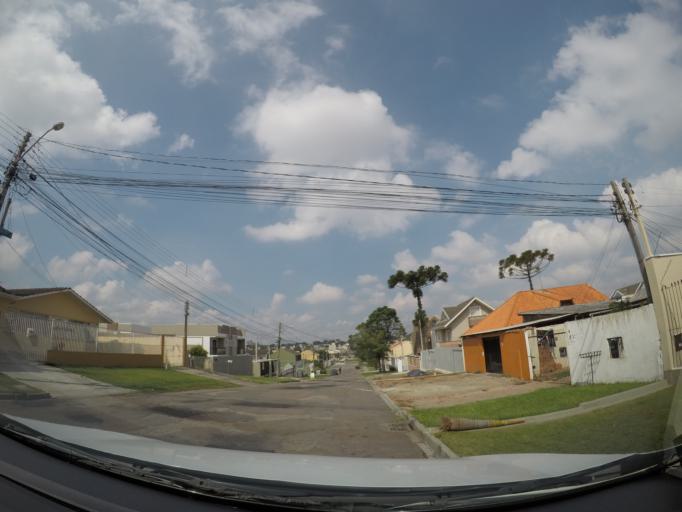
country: BR
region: Parana
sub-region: Sao Jose Dos Pinhais
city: Sao Jose dos Pinhais
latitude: -25.4886
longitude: -49.2549
